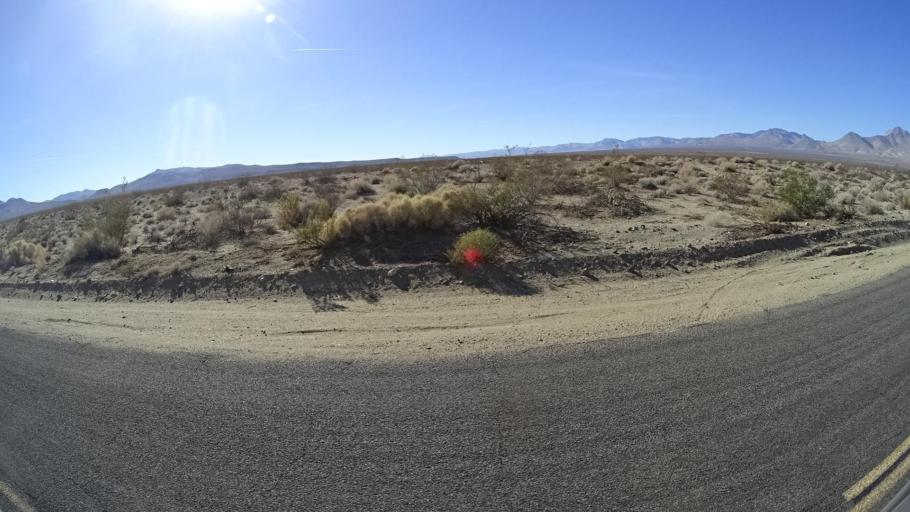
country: US
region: California
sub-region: Kern County
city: China Lake Acres
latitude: 35.5897
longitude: -117.7927
